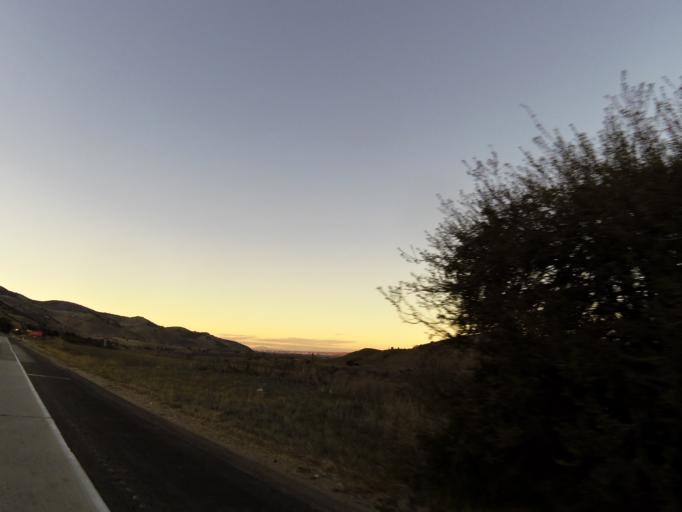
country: US
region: California
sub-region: San Luis Obispo County
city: Lake Nacimiento
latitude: 35.9148
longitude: -120.8551
